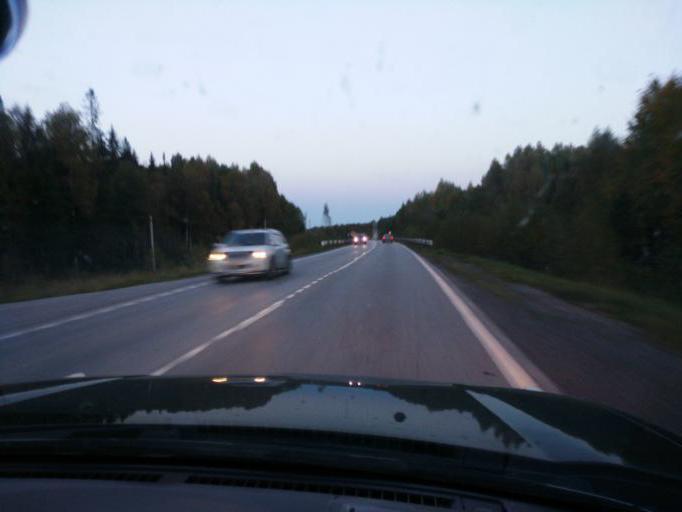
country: RU
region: Perm
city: Verkhnechusovskiye Gorodki
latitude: 58.2473
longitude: 57.0209
